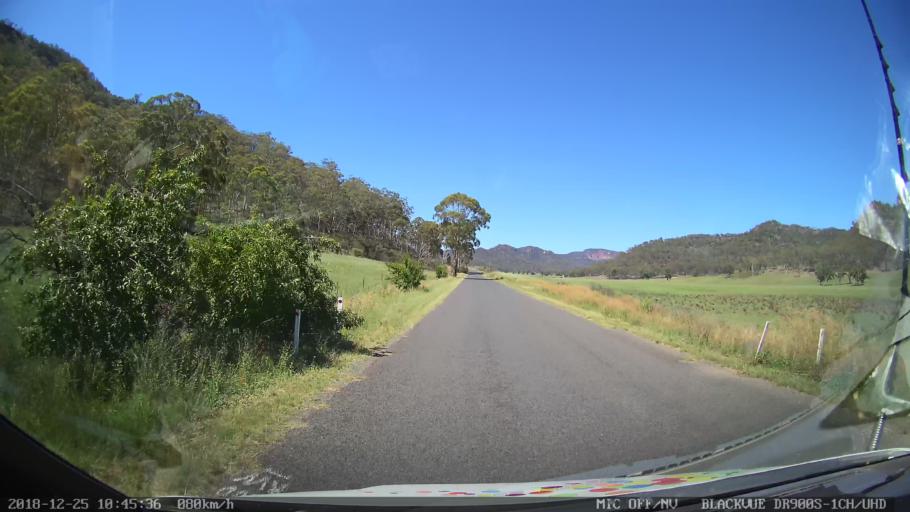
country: AU
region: New South Wales
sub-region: Upper Hunter Shire
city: Merriwa
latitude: -32.4350
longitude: 150.2890
